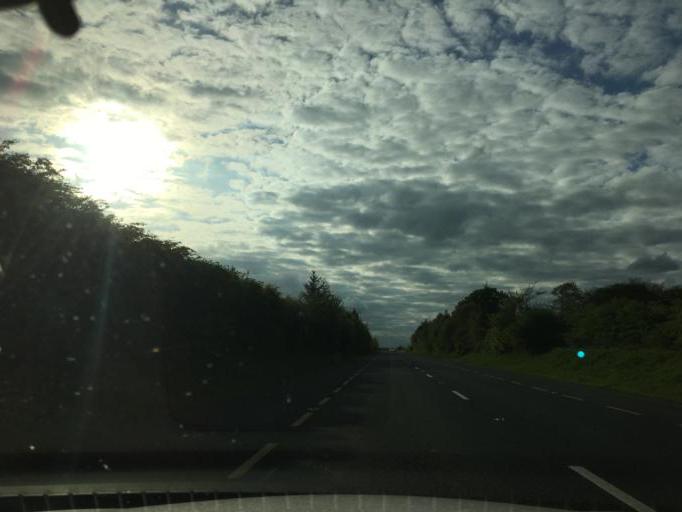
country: IE
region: Leinster
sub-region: Loch Garman
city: Enniscorthy
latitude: 52.3583
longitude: -6.7038
